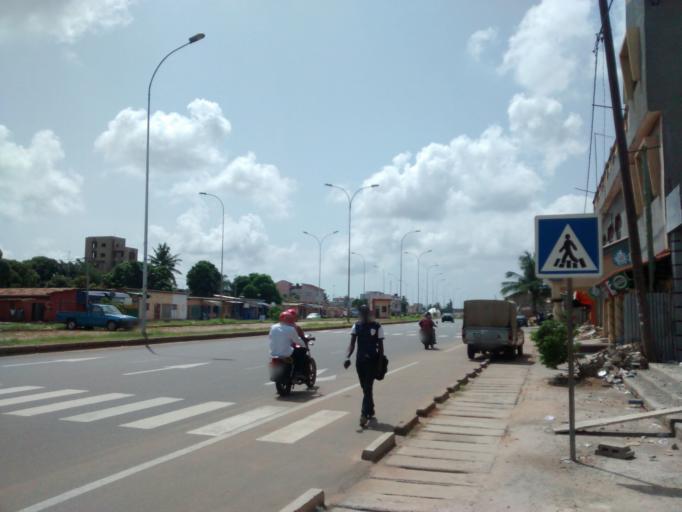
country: TG
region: Maritime
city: Lome
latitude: 6.2022
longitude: 1.1923
